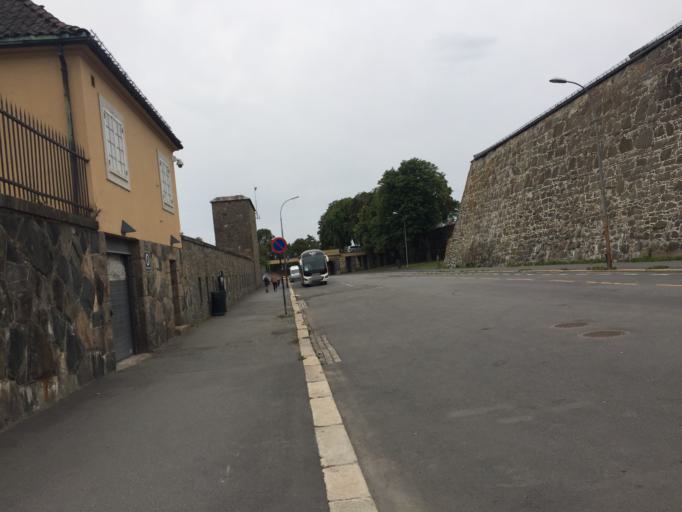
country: NO
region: Oslo
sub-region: Oslo
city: Oslo
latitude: 59.9078
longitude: 10.7396
